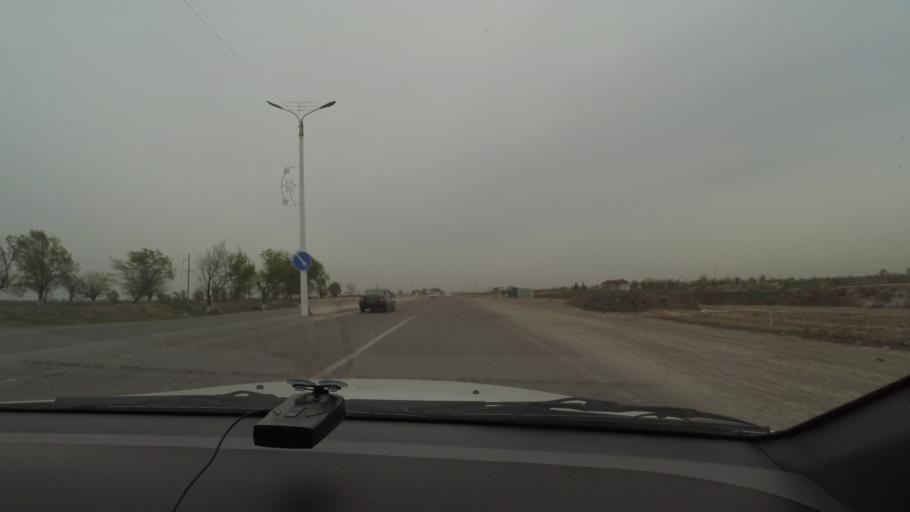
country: KZ
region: Ongtustik Qazaqstan
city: Myrzakent
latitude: 40.5371
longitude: 68.4269
